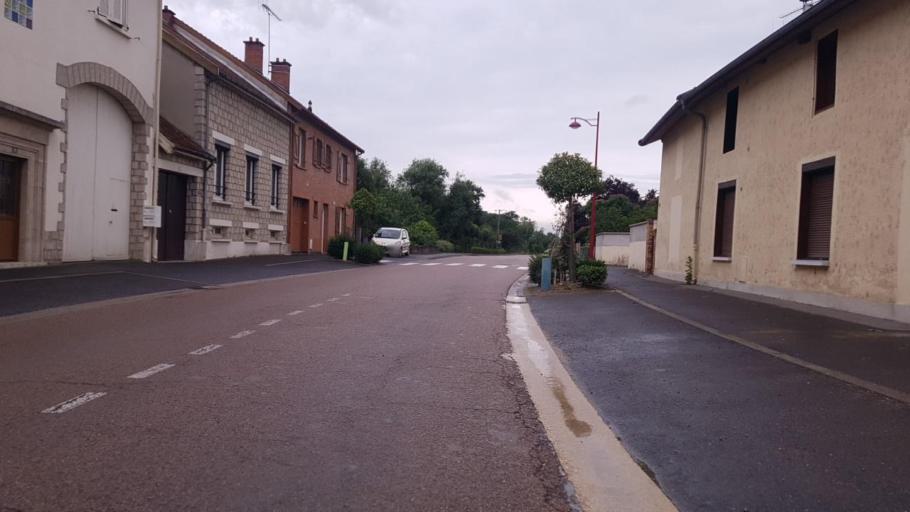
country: FR
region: Champagne-Ardenne
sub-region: Departement de la Marne
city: Vitry-le-Francois
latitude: 48.7431
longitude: 4.6255
